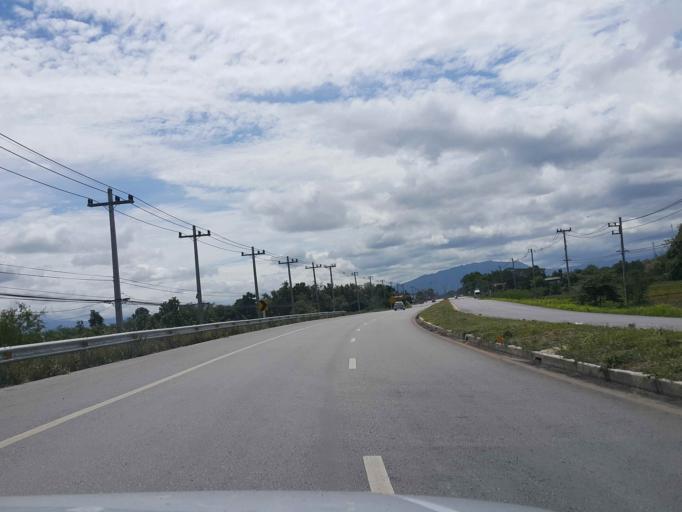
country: TH
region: Tak
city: Tak
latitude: 16.8849
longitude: 99.2040
